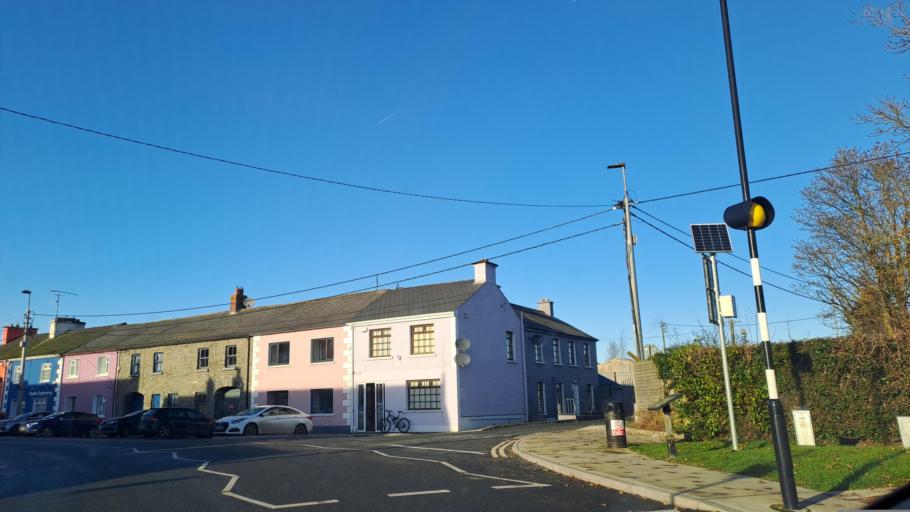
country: IE
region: Ulster
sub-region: An Cabhan
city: Mullagh
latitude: 53.8114
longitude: -6.9440
